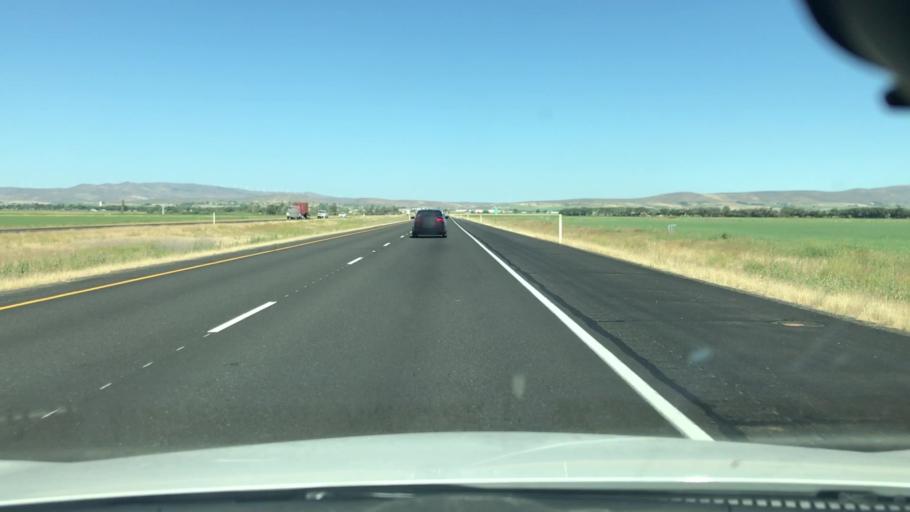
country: US
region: Washington
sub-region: Kittitas County
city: Kittitas
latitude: 46.9701
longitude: -120.4669
